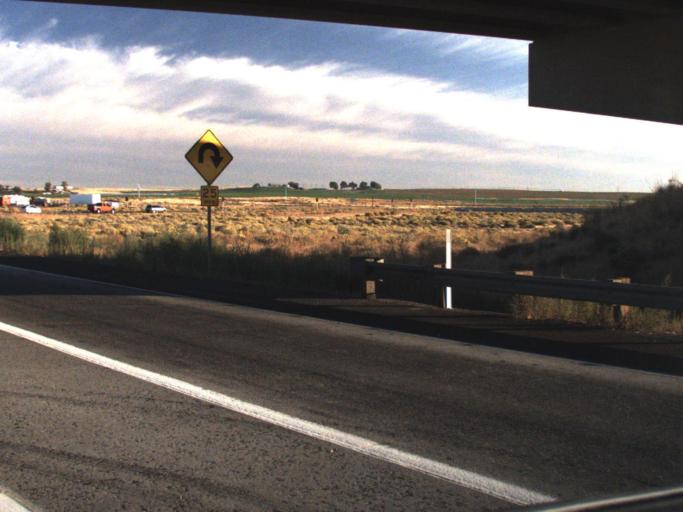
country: US
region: Washington
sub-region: Franklin County
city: Pasco
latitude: 46.2649
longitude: -119.0865
